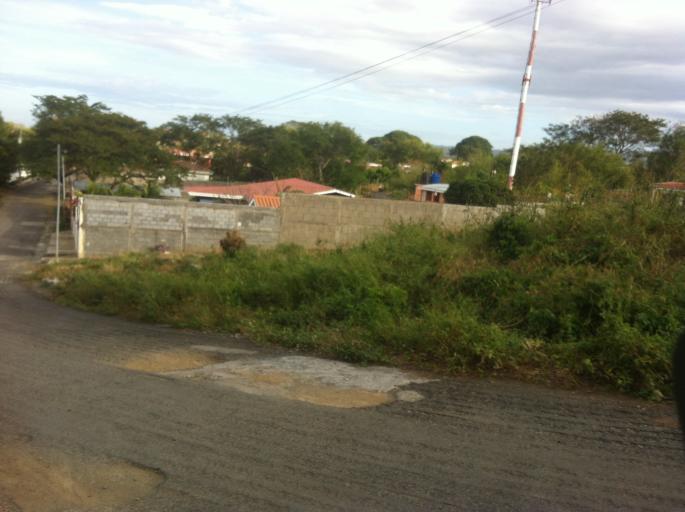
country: NI
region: Managua
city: Ciudad Sandino
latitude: 12.1005
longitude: -86.3261
